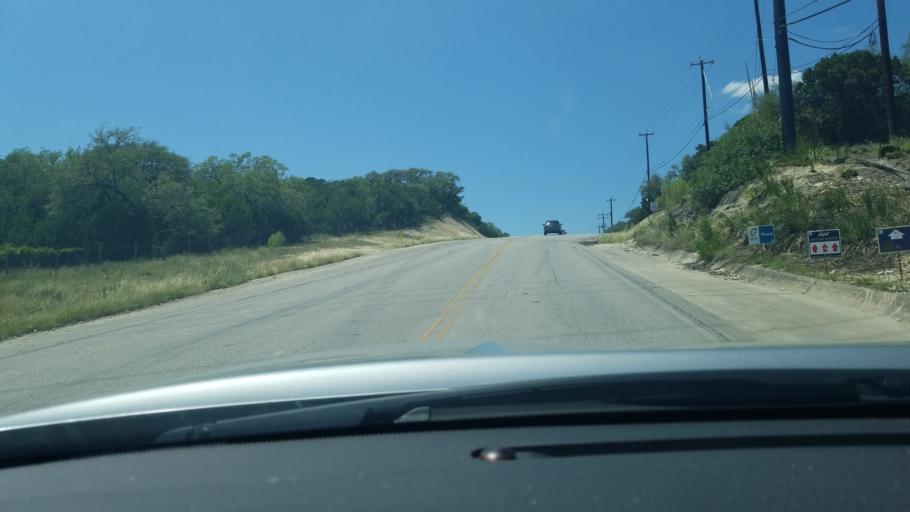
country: US
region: Texas
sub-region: Bexar County
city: Timberwood Park
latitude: 29.7107
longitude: -98.4494
